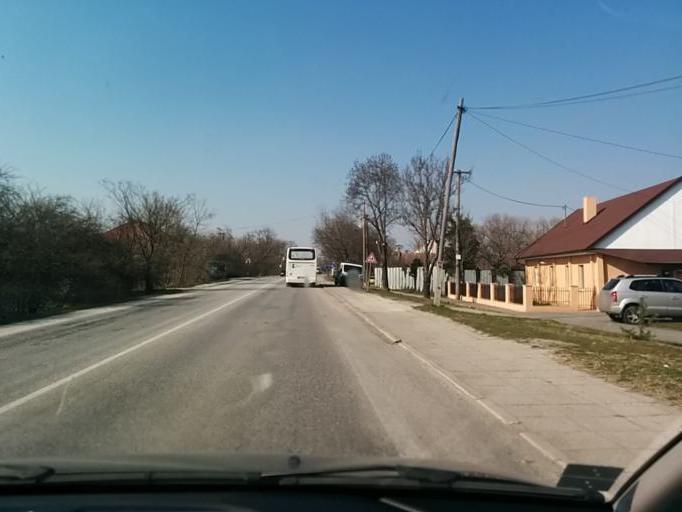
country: SK
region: Trnavsky
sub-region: Okres Galanta
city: Galanta
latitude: 48.2194
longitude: 17.7286
